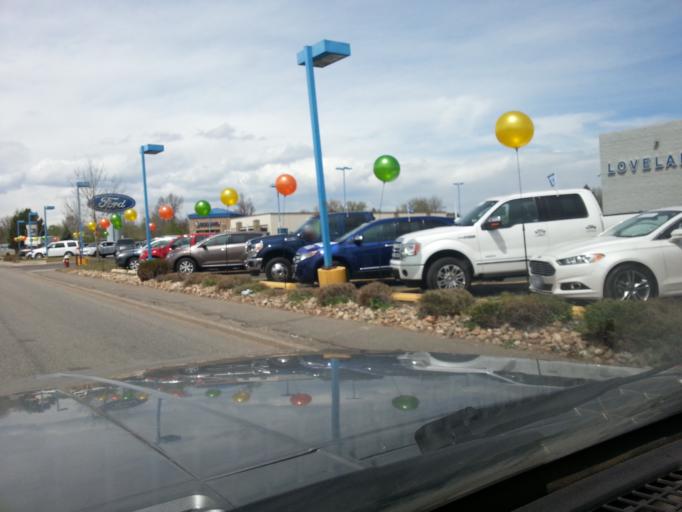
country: US
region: Colorado
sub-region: Larimer County
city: Loveland
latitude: 40.4074
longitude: -105.0637
